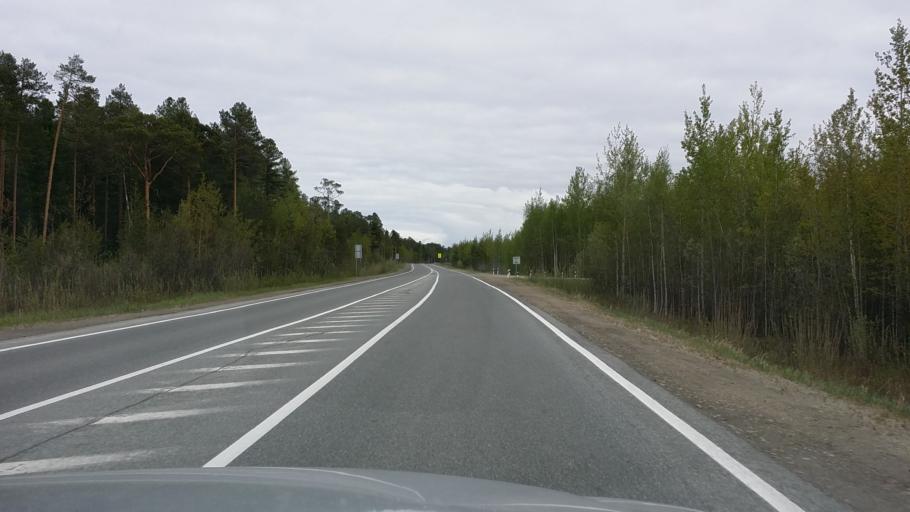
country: RU
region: Khanty-Mansiyskiy Avtonomnyy Okrug
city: Langepas
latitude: 61.2207
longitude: 75.3378
